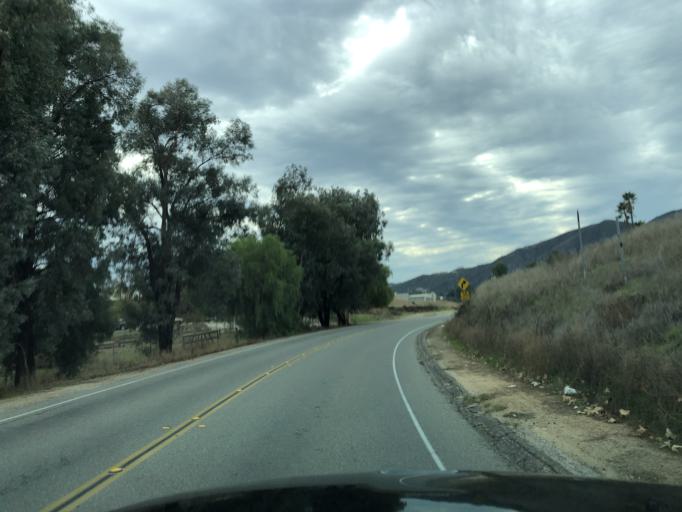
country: US
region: California
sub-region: Riverside County
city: Wildomar
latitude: 33.6095
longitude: -117.2749
